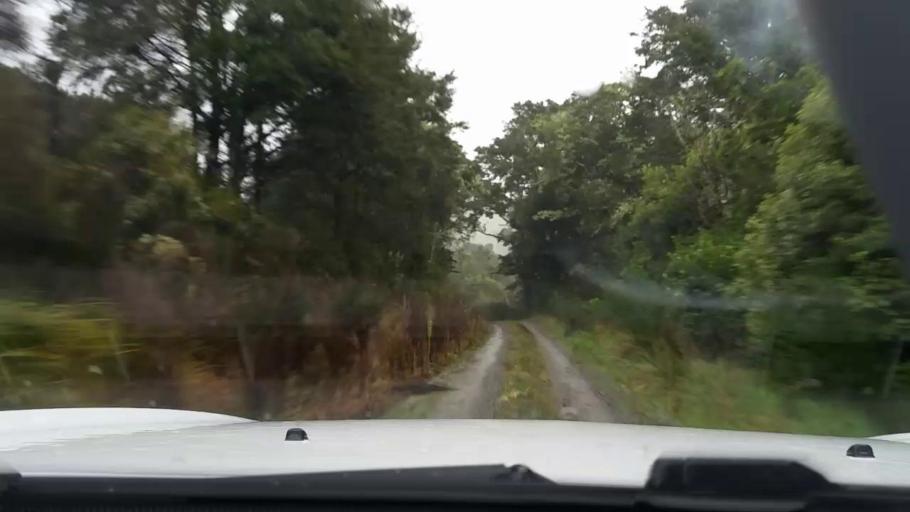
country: NZ
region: Wellington
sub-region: Masterton District
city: Masterton
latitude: -41.1601
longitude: 175.7973
